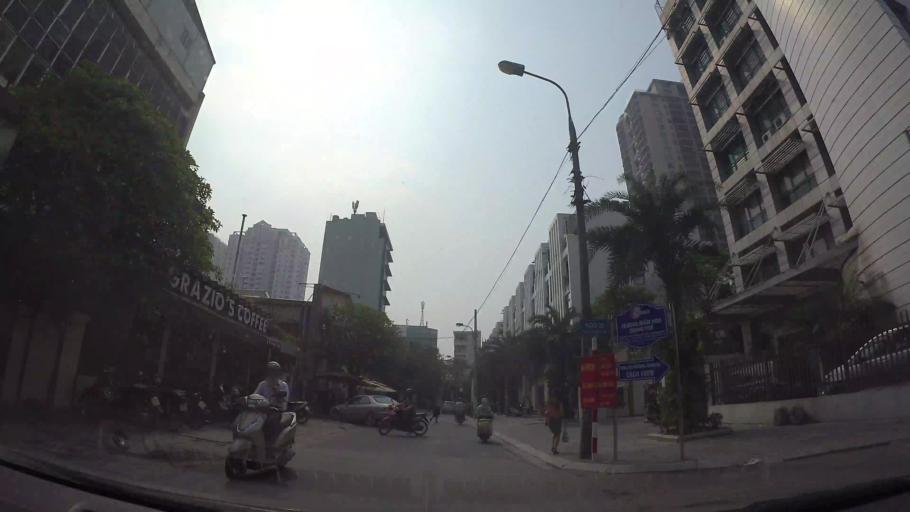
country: VN
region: Ha Noi
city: Dong Da
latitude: 21.0140
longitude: 105.8110
